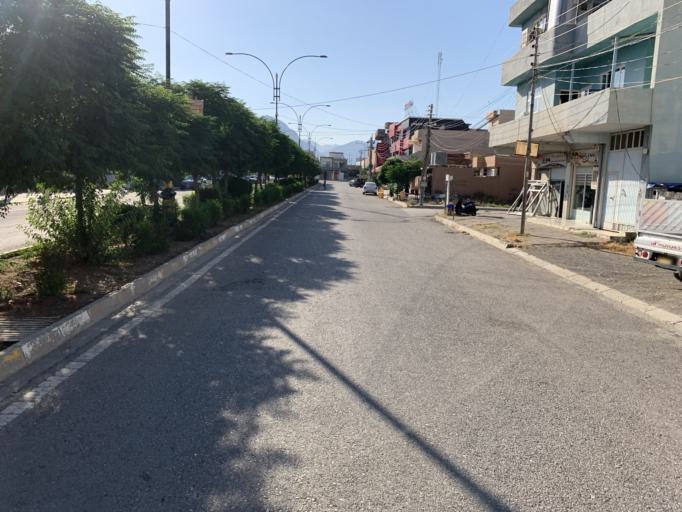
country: IQ
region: As Sulaymaniyah
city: Raniye
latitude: 36.2417
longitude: 44.8738
